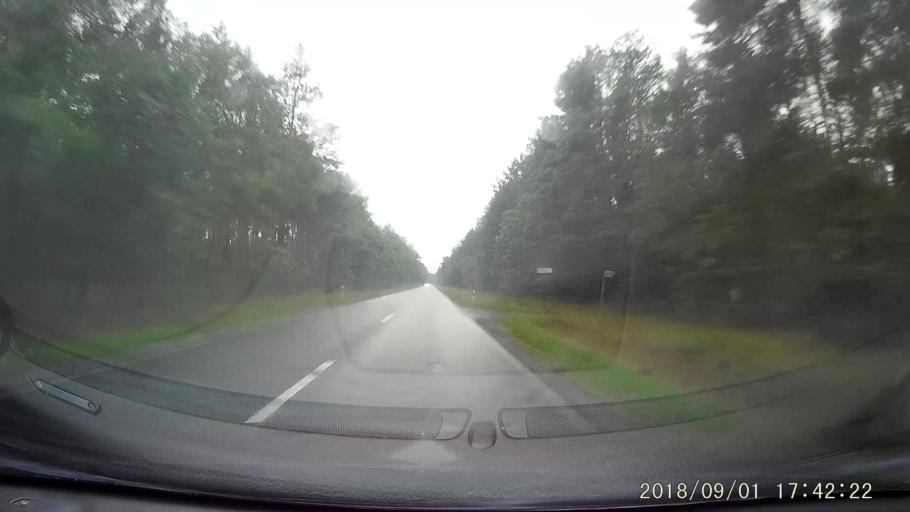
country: PL
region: Lubusz
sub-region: Powiat zaganski
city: Zagan
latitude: 51.5572
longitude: 15.2600
